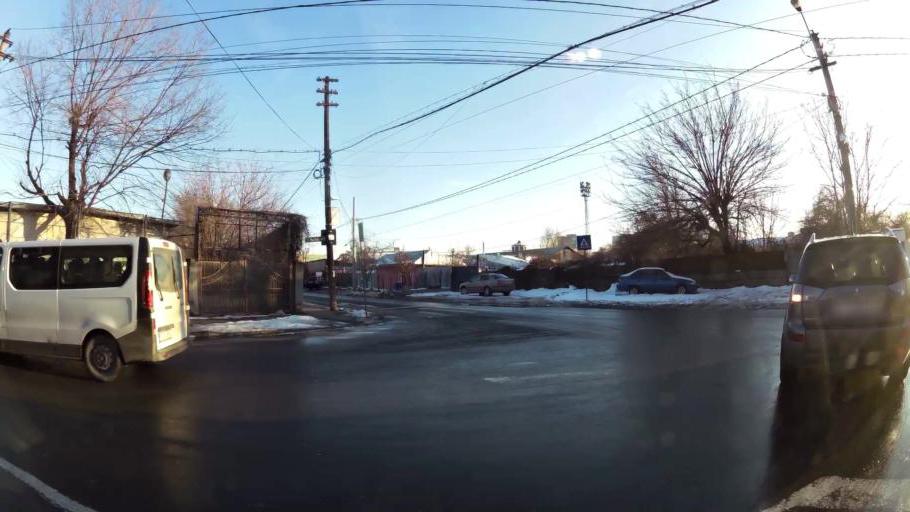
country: RO
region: Ilfov
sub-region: Comuna Fundeni-Dobroesti
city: Fundeni
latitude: 44.4514
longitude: 26.1377
